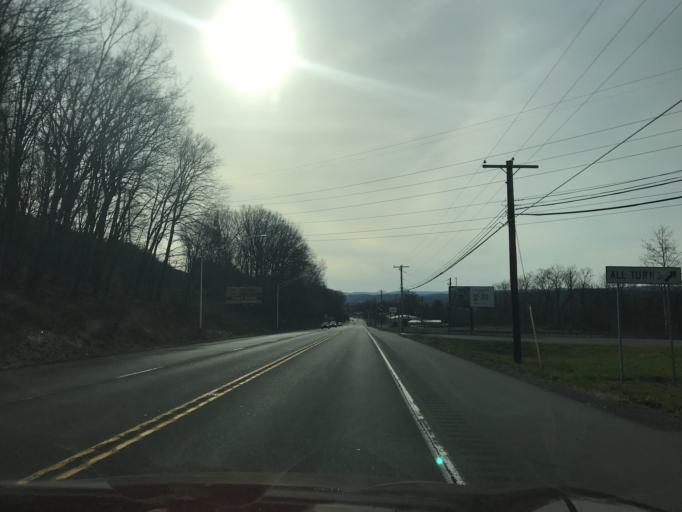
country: US
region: Pennsylvania
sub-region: Lycoming County
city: Kenmar
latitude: 41.2282
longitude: -76.9592
